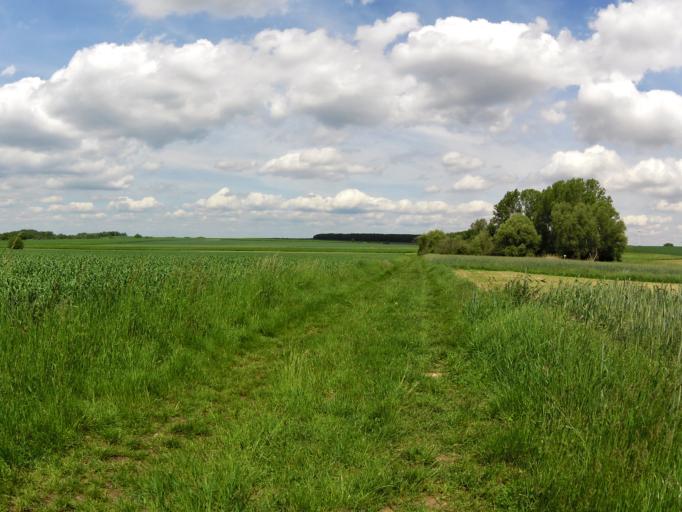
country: DE
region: Bavaria
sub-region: Regierungsbezirk Unterfranken
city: Theilheim
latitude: 49.7276
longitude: 10.0353
